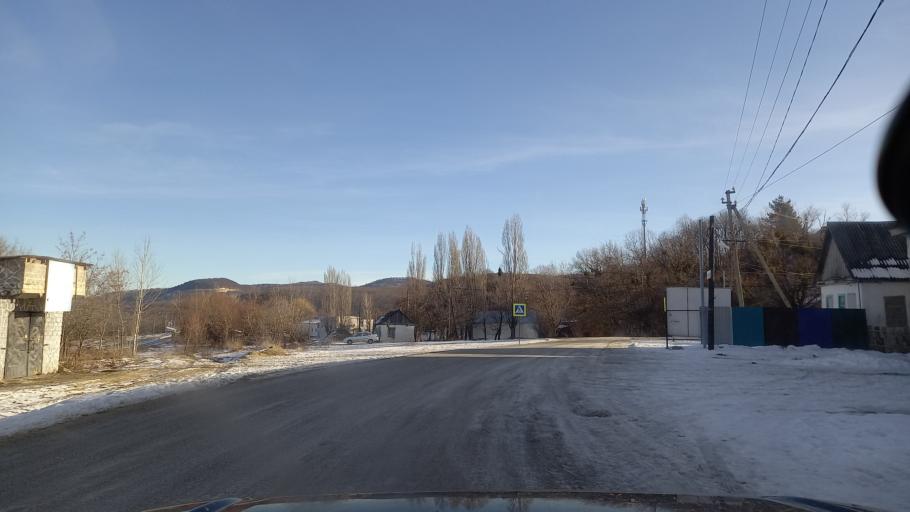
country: RU
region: Adygeya
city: Kamennomostskiy
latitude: 44.2911
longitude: 40.1837
